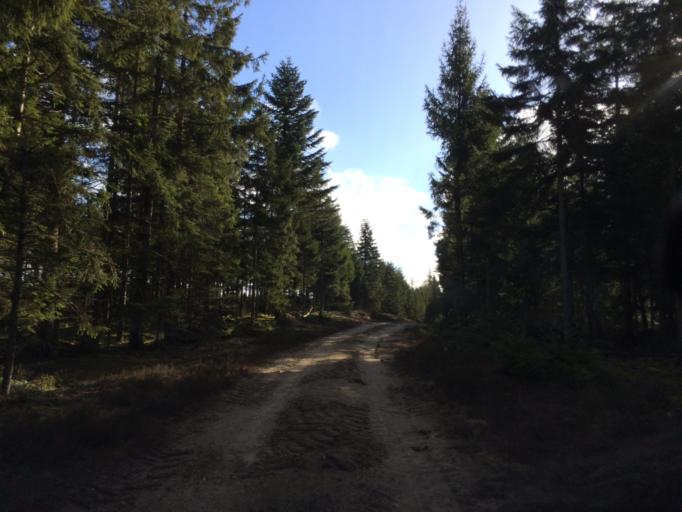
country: DK
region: Central Jutland
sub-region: Holstebro Kommune
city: Ulfborg
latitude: 56.2516
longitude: 8.4384
